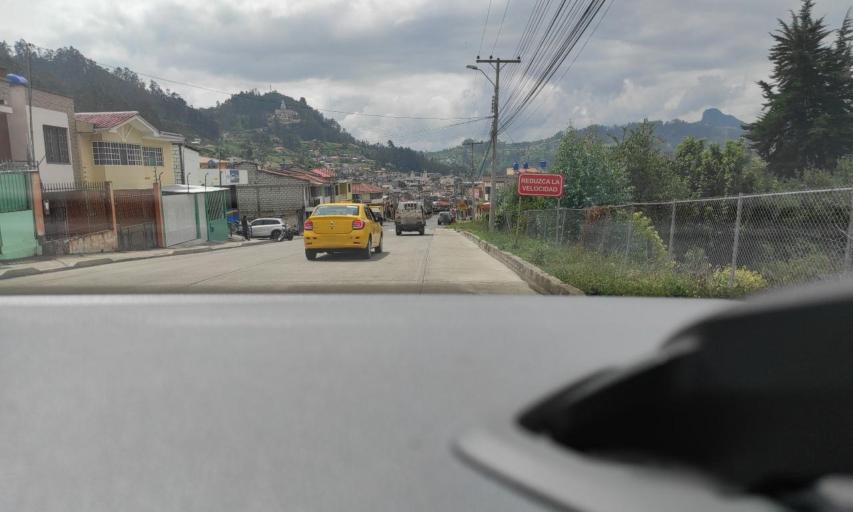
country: EC
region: Canar
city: Azogues
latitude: -2.7067
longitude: -78.8920
